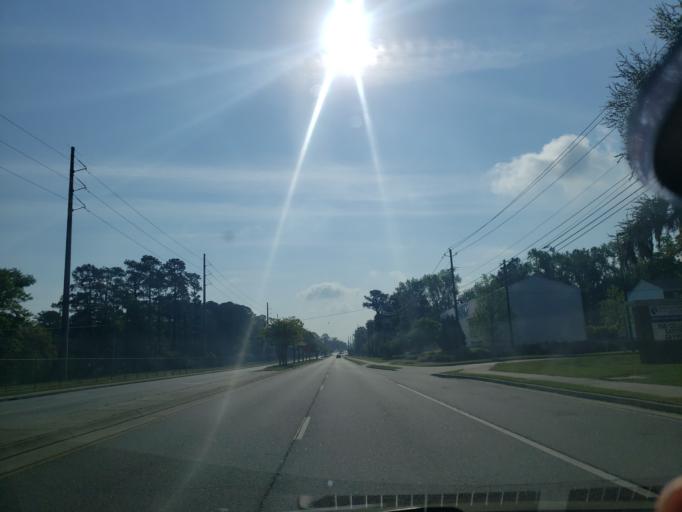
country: US
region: Georgia
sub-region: Chatham County
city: Montgomery
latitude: 32.0026
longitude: -81.1348
